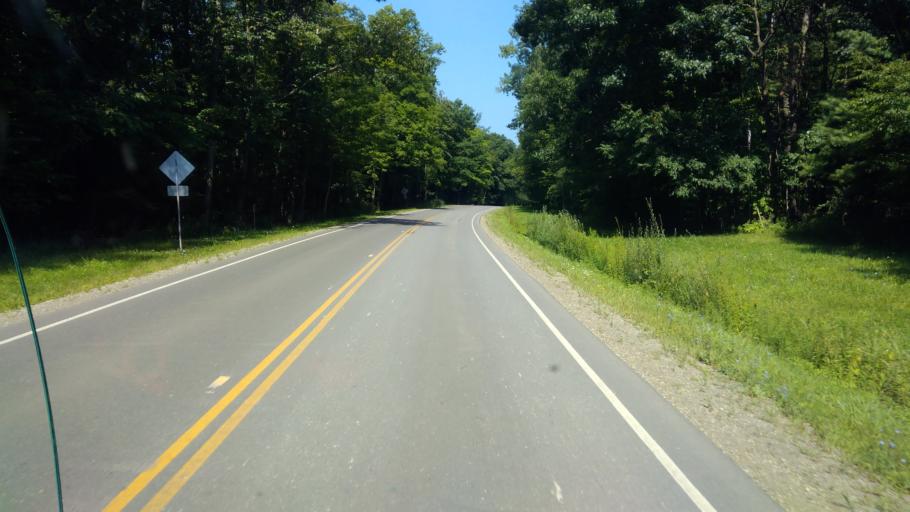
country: US
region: New York
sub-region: Allegany County
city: Belmont
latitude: 42.2630
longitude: -78.0398
